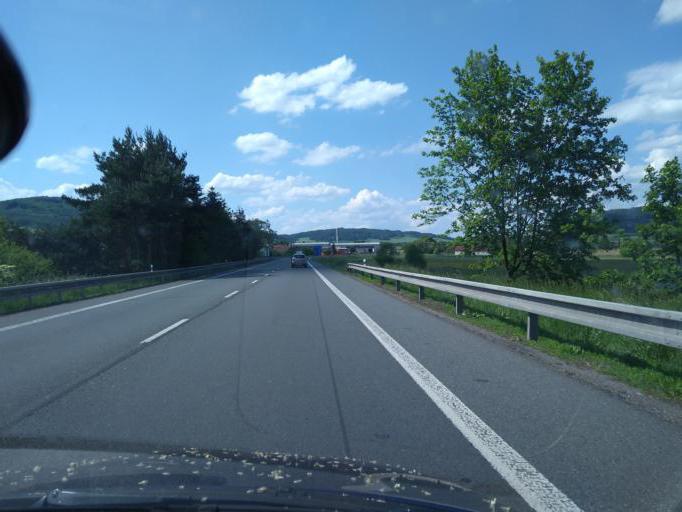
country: CZ
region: Plzensky
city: Svihov
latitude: 49.4854
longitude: 13.2862
